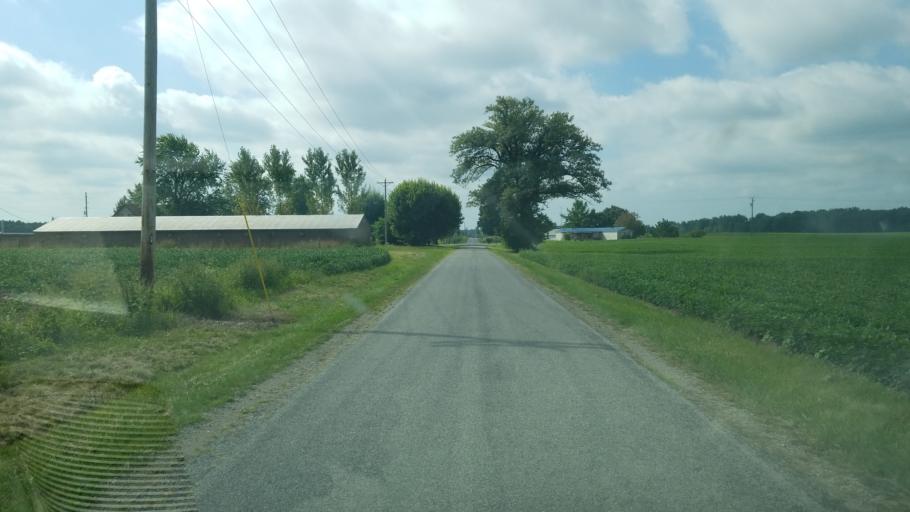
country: US
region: Ohio
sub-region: Union County
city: Richwood
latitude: 40.6017
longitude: -83.3617
